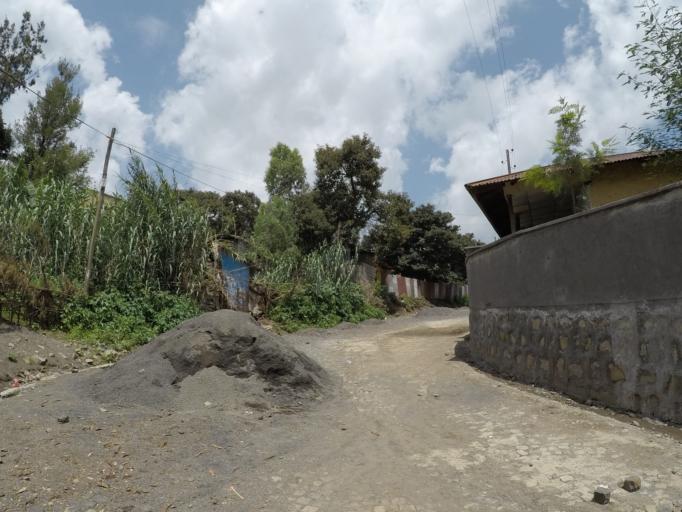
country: ET
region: Amhara
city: Gondar
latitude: 12.6138
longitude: 37.4730
